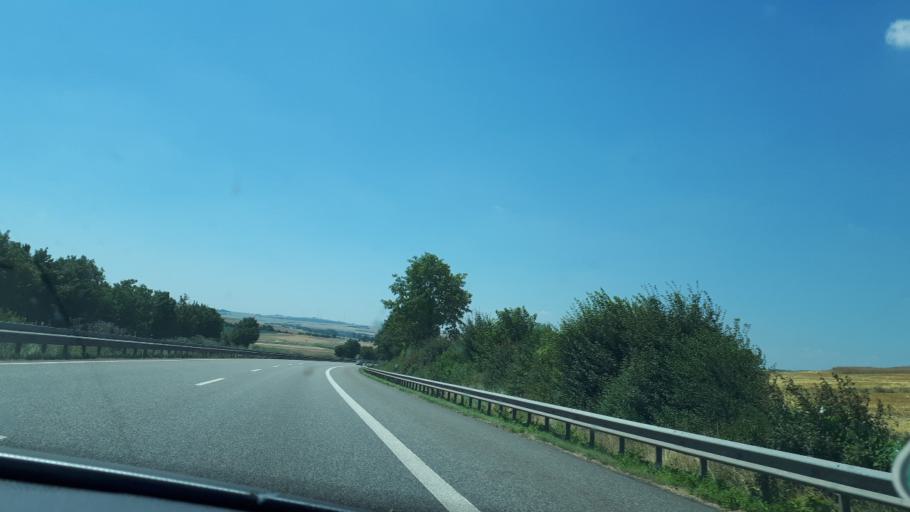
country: DE
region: Rheinland-Pfalz
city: Kerben
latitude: 50.3202
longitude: 7.3630
